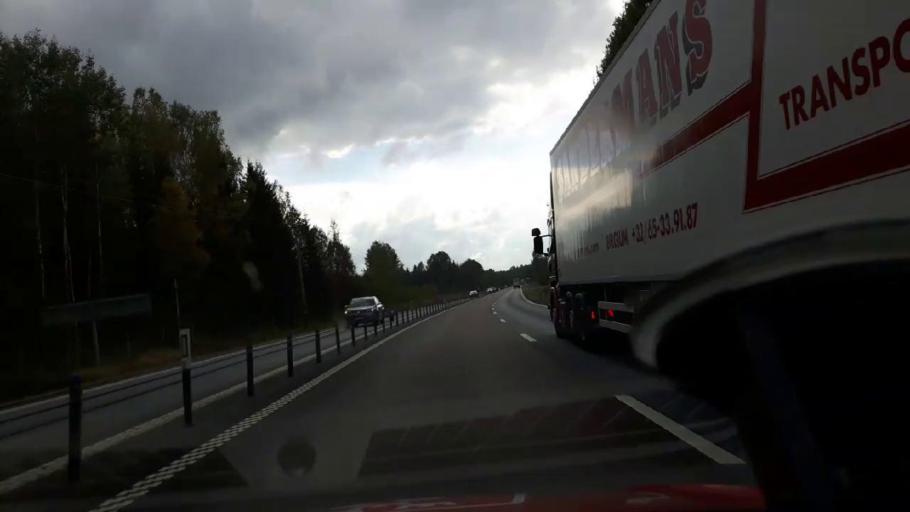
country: SE
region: Gaevleborg
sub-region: Gavle Kommun
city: Norrsundet
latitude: 60.9581
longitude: 17.0346
